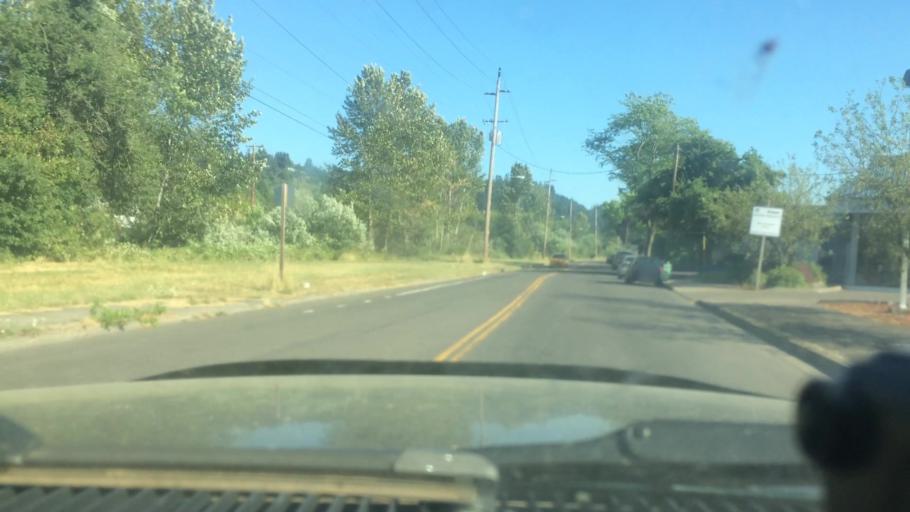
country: US
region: Oregon
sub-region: Lane County
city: Eugene
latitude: 44.0200
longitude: -123.0811
